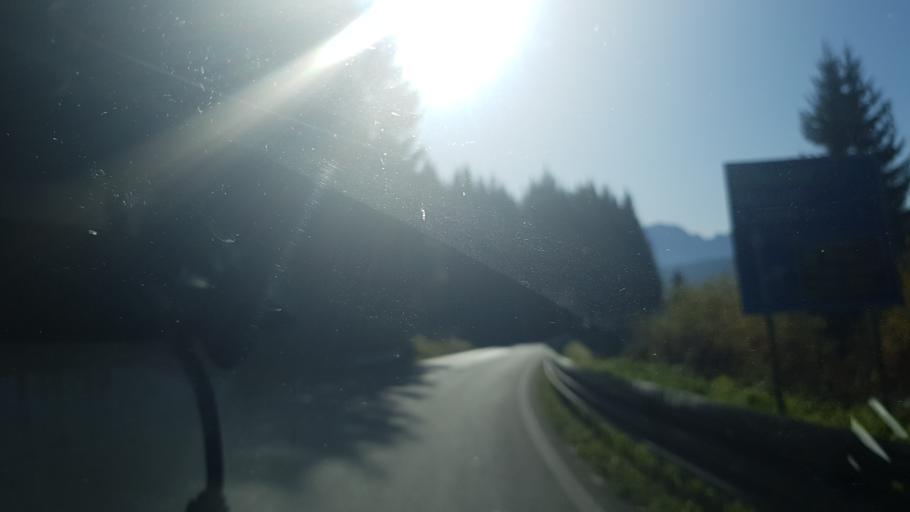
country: IT
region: Veneto
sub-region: Provincia di Belluno
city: Candide
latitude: 46.6241
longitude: 12.4702
